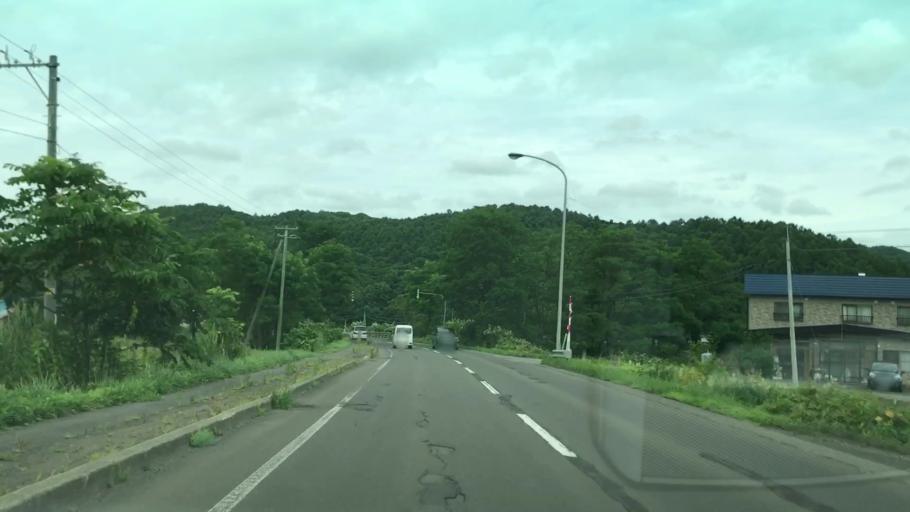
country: JP
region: Hokkaido
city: Iwanai
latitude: 42.9635
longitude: 140.6924
